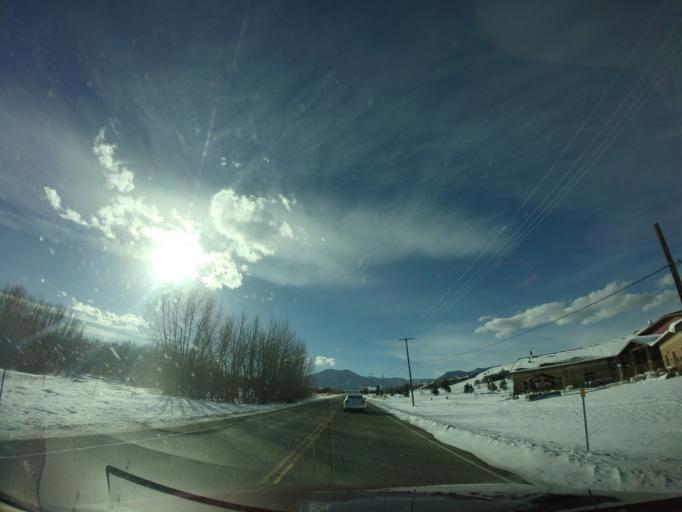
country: US
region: Montana
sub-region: Carbon County
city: Red Lodge
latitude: 45.2112
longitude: -109.2433
